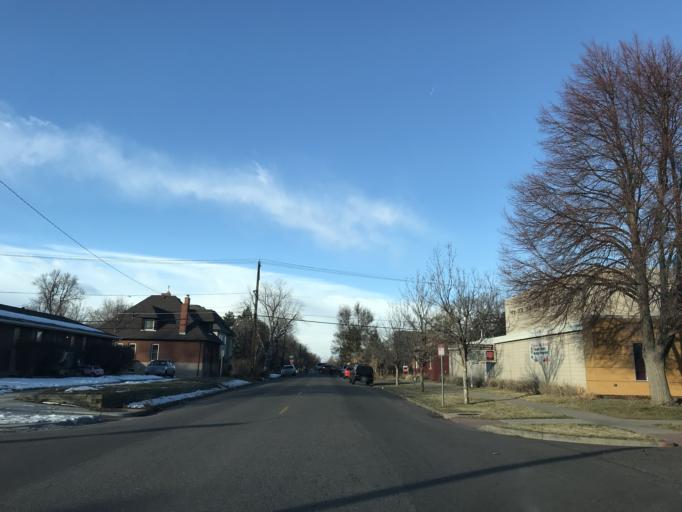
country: US
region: Colorado
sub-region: Denver County
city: Denver
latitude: 39.7583
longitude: -104.9646
